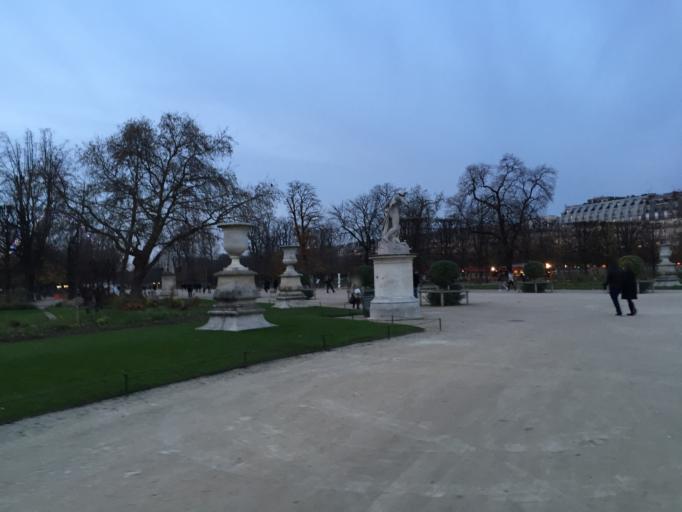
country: FR
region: Ile-de-France
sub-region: Paris
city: Paris
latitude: 48.8628
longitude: 2.3288
